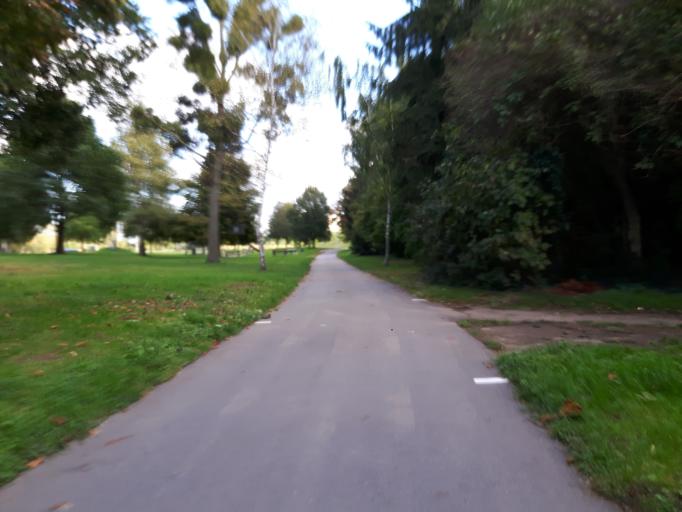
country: DE
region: Baden-Wuerttemberg
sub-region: Regierungsbezirk Stuttgart
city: Offenau
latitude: 49.2327
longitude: 9.1815
